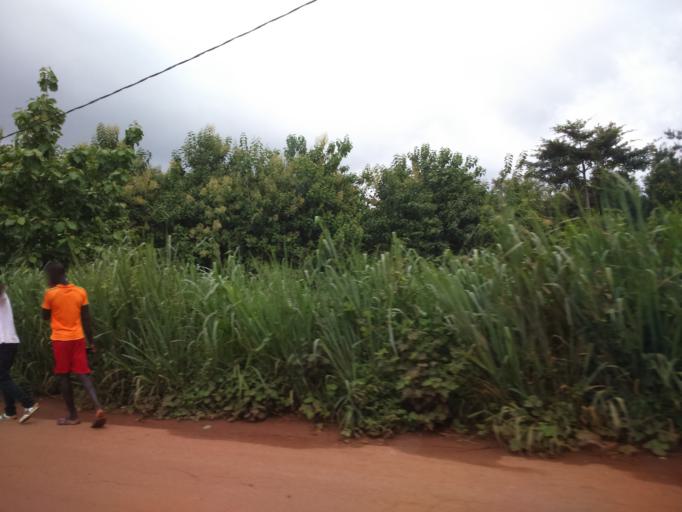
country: CI
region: Moyen-Comoe
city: Abengourou
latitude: 6.6368
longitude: -3.7119
